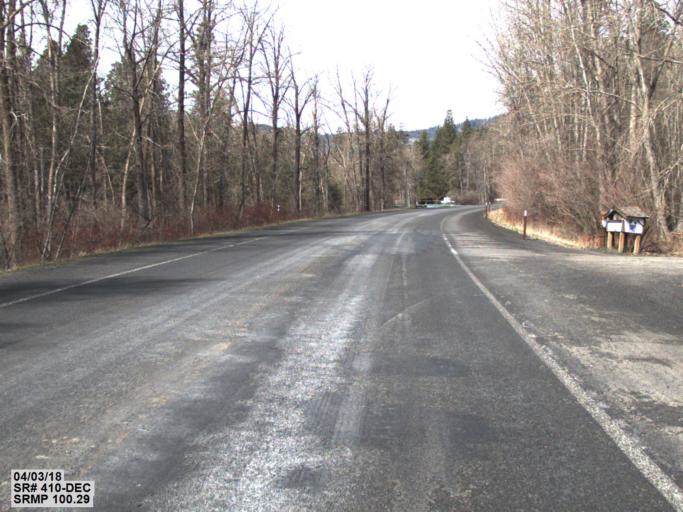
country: US
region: Washington
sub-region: Kittitas County
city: Cle Elum
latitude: 46.8991
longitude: -121.0097
